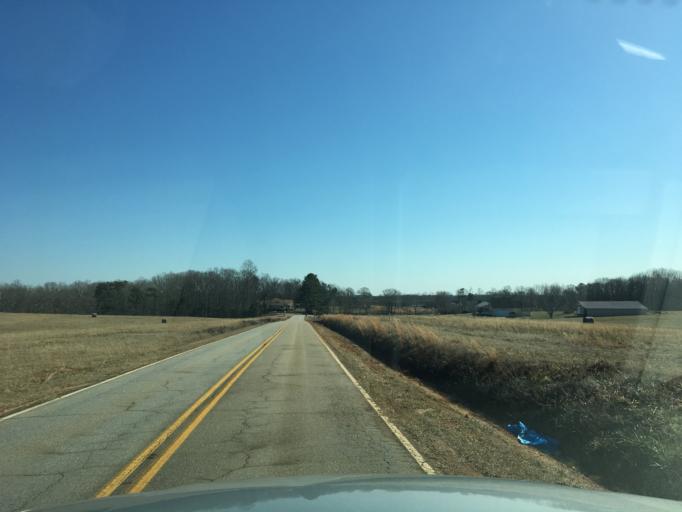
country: US
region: South Carolina
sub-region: Pickens County
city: Liberty
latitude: 34.8184
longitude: -82.7750
